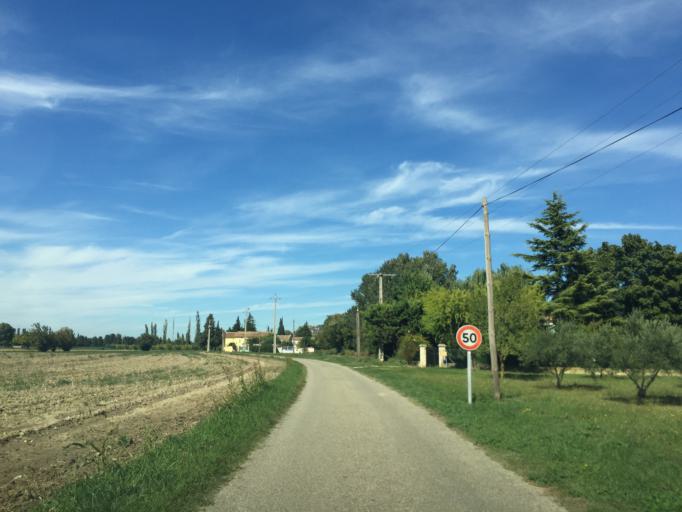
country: FR
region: Provence-Alpes-Cote d'Azur
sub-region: Departement du Vaucluse
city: Mornas
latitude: 44.1804
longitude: 4.7355
